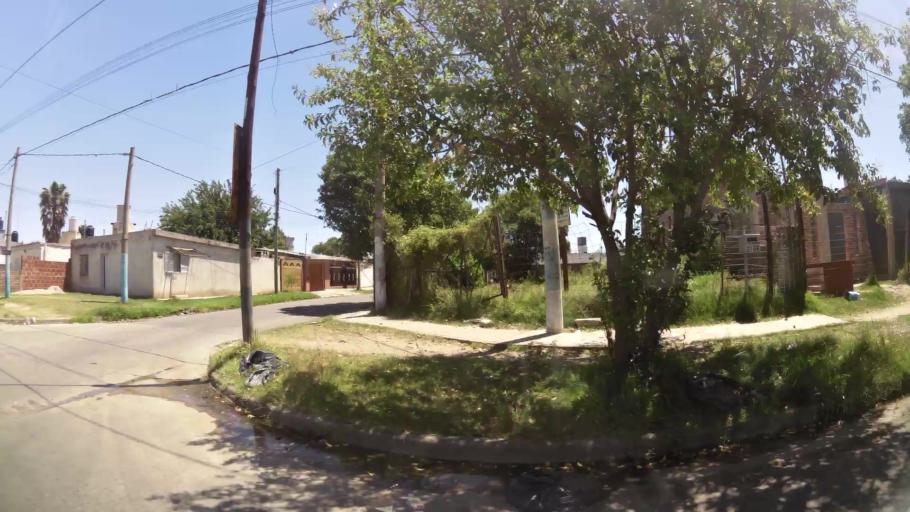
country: AR
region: Cordoba
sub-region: Departamento de Capital
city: Cordoba
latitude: -31.3854
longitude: -64.1428
